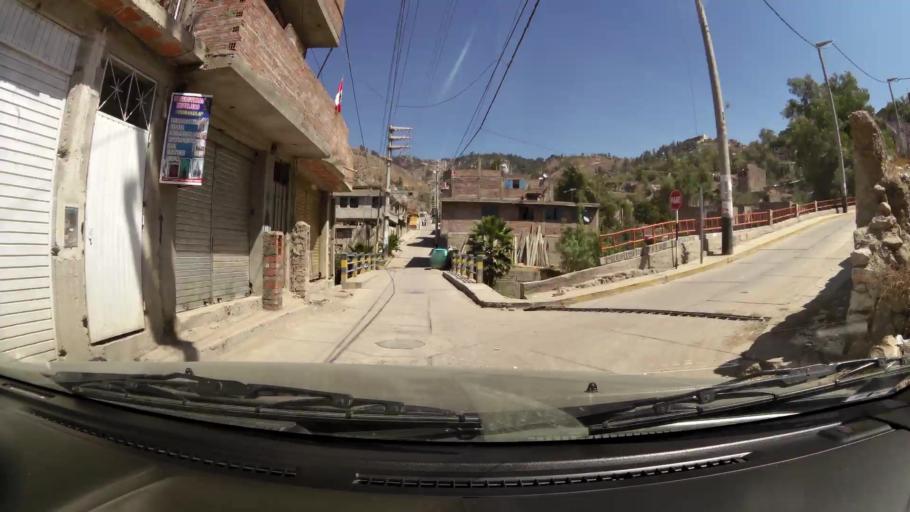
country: PE
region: Ayacucho
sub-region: Provincia de Huamanga
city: Ayacucho
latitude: -13.1673
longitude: -74.2315
